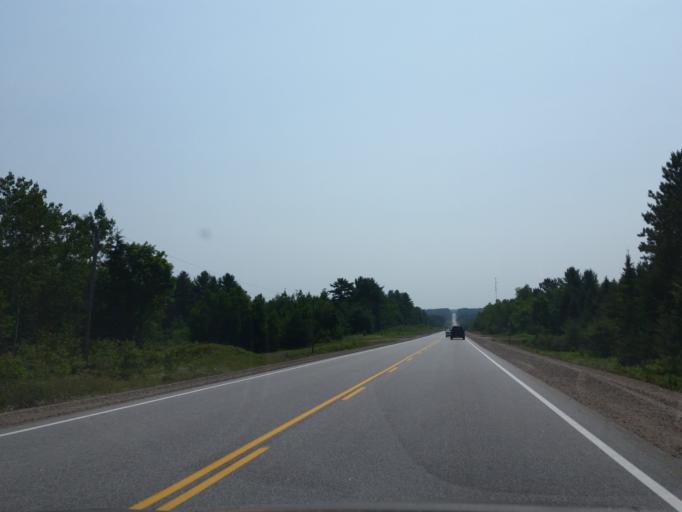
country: CA
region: Ontario
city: Mattawa
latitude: 46.2967
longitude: -78.5480
